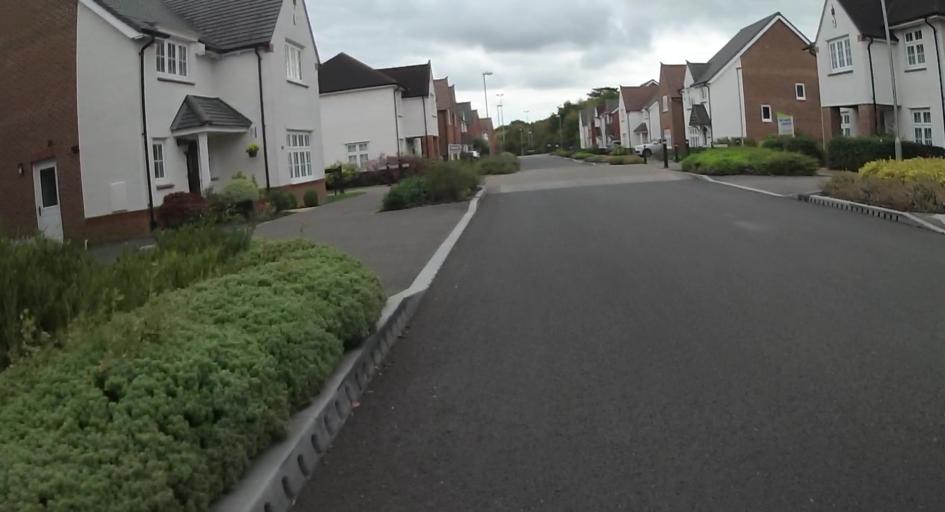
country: GB
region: England
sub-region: Bracknell Forest
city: Binfield
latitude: 51.4008
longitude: -0.7840
